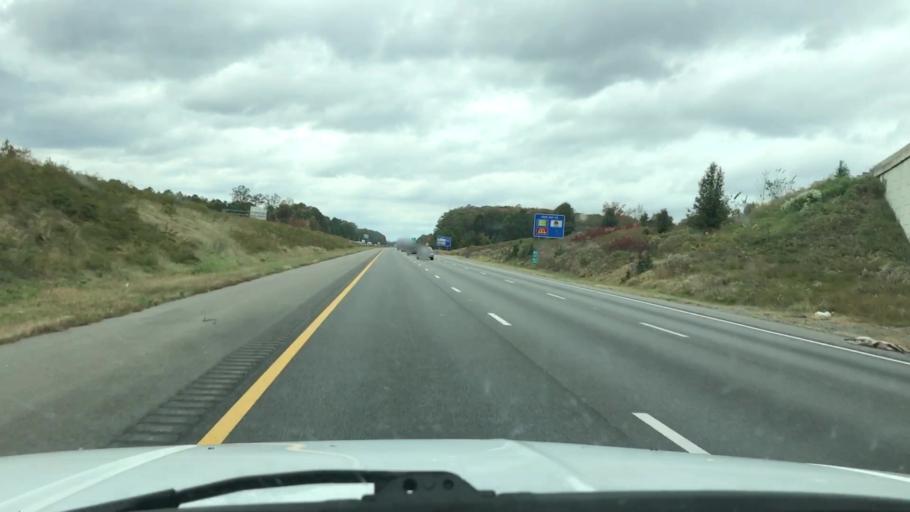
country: US
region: Virginia
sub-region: Henrico County
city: Short Pump
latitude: 37.6732
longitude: -77.6512
